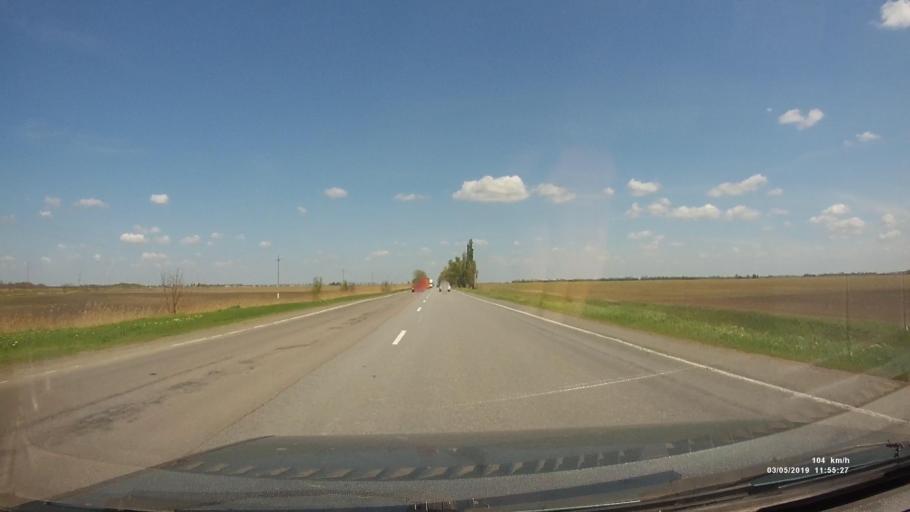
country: RU
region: Rostov
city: Bagayevskaya
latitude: 47.1811
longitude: 40.2912
